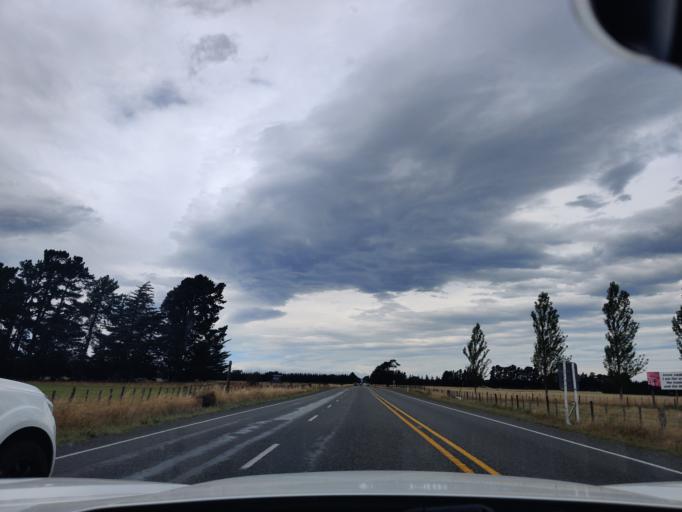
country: NZ
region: Wellington
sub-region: Masterton District
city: Masterton
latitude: -40.9963
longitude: 175.5622
